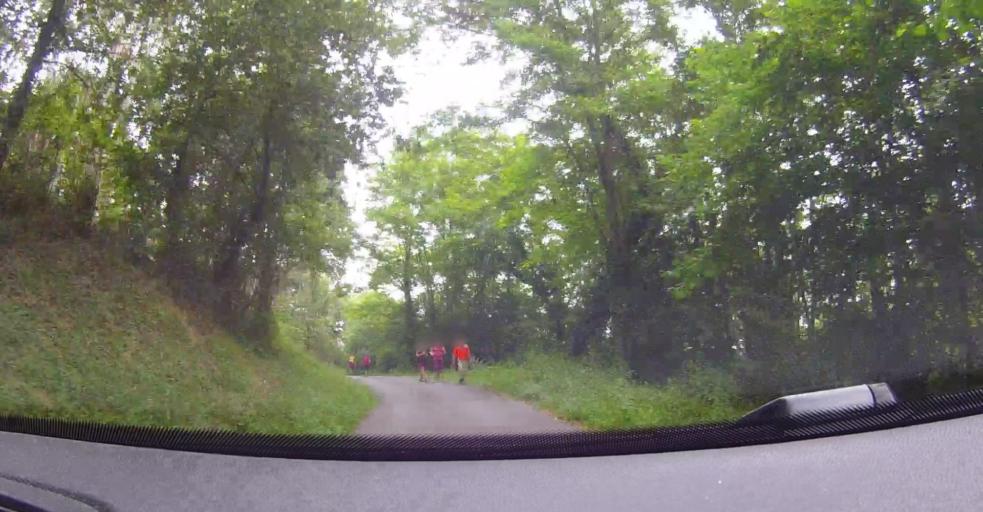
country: ES
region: Basque Country
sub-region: Bizkaia
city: Sopuerta
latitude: 43.2586
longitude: -3.1471
